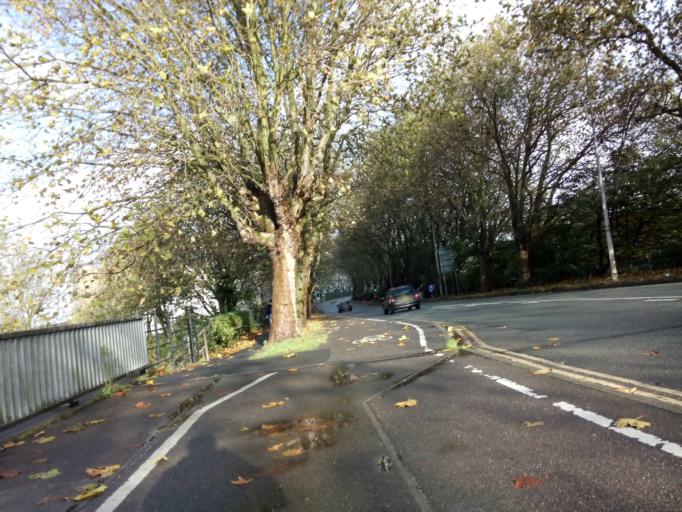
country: GB
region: England
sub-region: Suffolk
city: Ipswich
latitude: 52.0597
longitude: 1.1350
